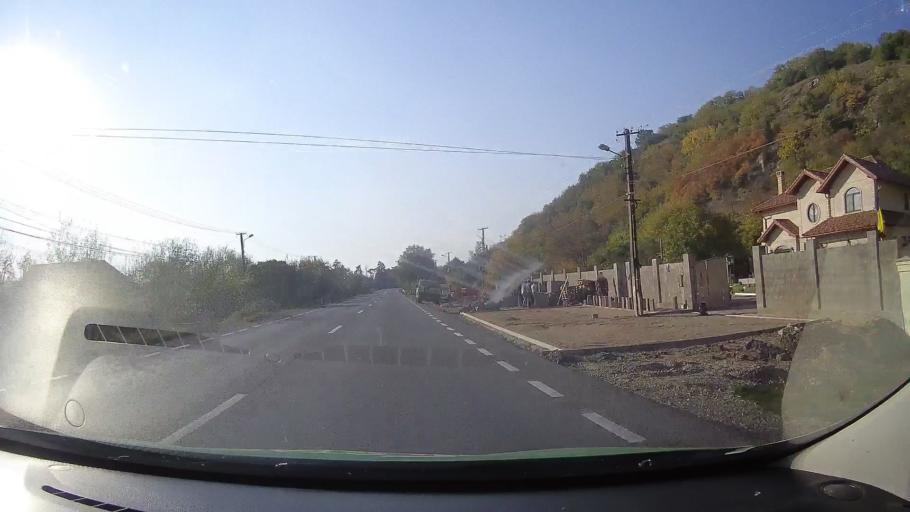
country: RO
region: Arad
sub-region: Comuna Paulis
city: Paulis
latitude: 46.1088
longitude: 21.6051
